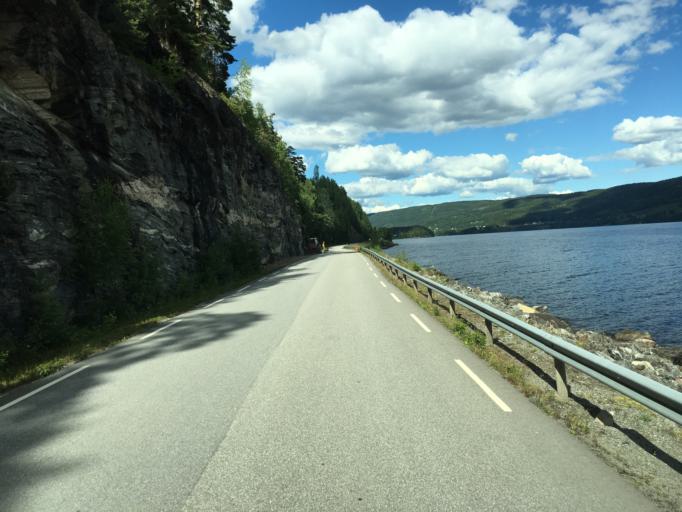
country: NO
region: Oppland
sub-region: Sondre Land
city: Hov
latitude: 60.6020
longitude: 10.3233
